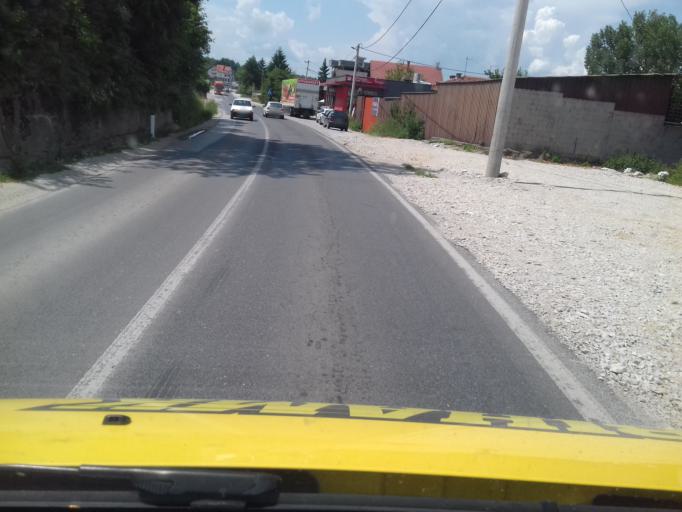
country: BA
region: Federation of Bosnia and Herzegovina
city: Hadzici
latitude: 43.8597
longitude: 18.2266
